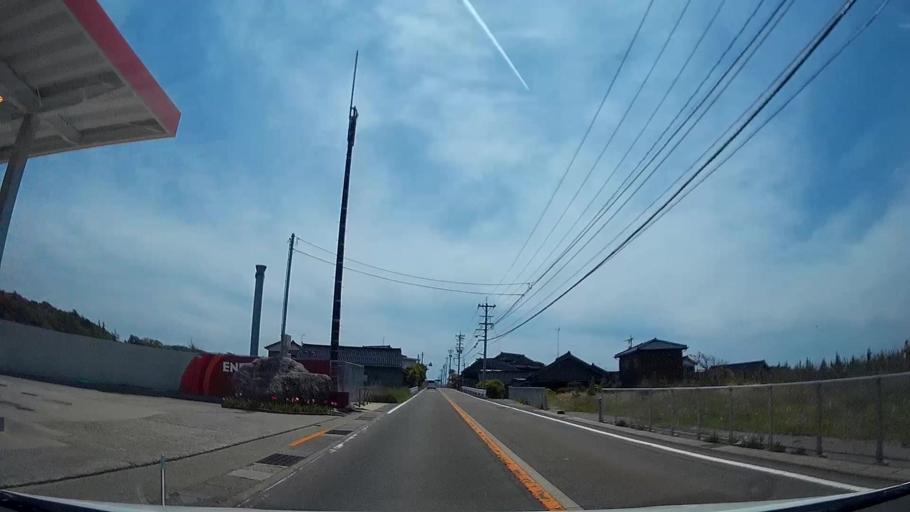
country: JP
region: Ishikawa
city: Hakui
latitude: 36.9434
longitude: 136.7629
